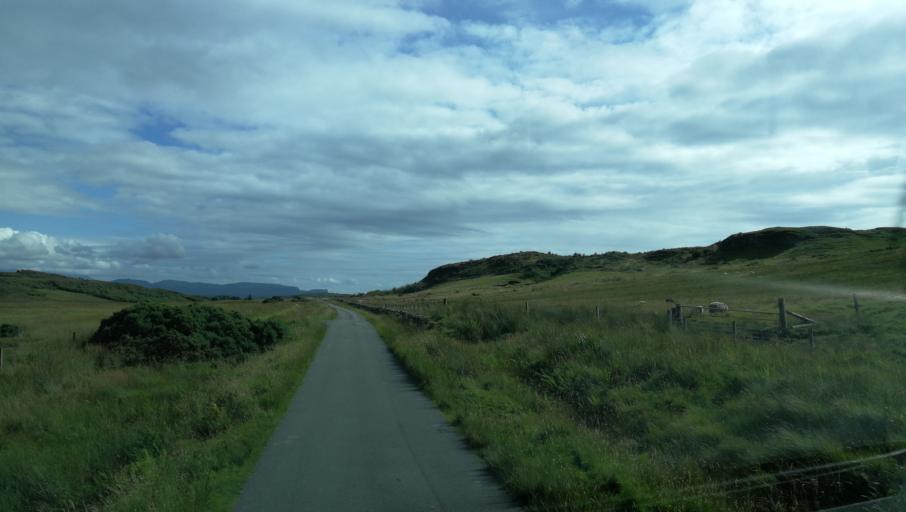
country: GB
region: Scotland
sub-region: Highland
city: Isle of Skye
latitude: 57.4059
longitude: -6.5703
